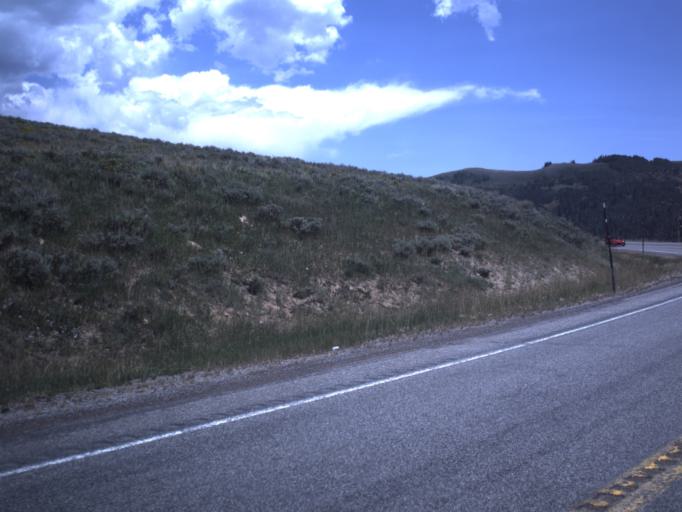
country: US
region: Utah
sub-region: Sanpete County
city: Fairview
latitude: 39.5820
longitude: -111.2462
